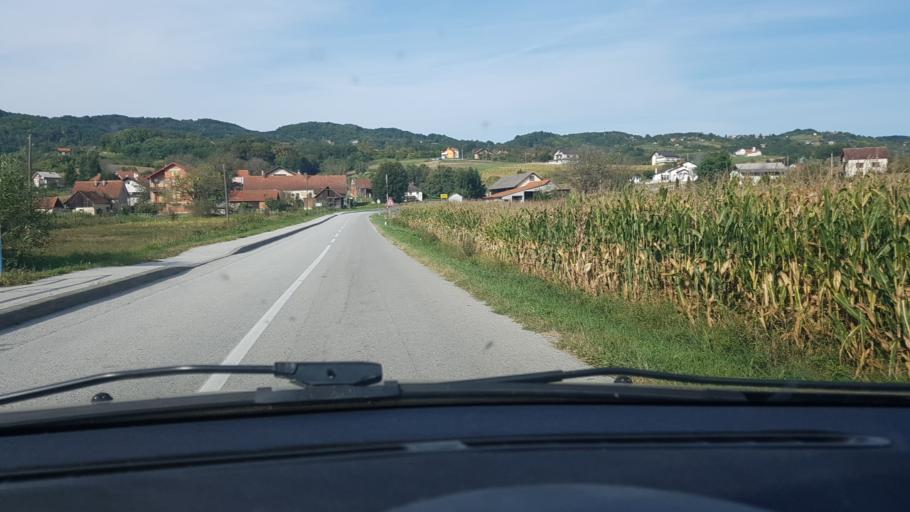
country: HR
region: Krapinsko-Zagorska
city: Mihovljan
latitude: 46.1494
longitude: 15.9597
